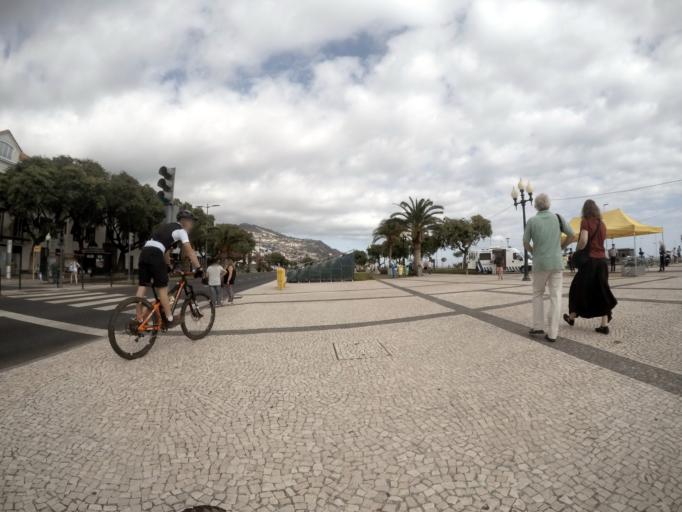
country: PT
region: Madeira
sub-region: Funchal
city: Funchal
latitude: 32.6469
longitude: -16.9069
